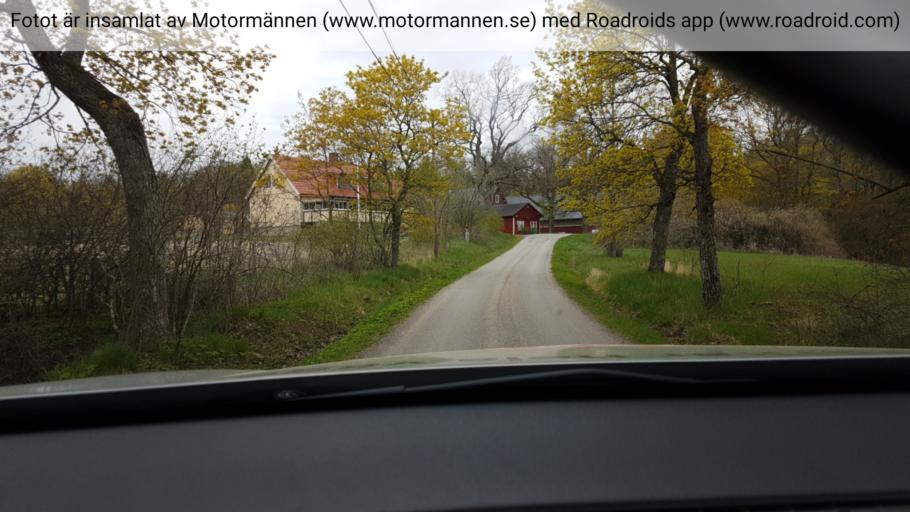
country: SE
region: Stockholm
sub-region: Haninge Kommun
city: Jordbro
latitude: 59.0139
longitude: 18.1151
